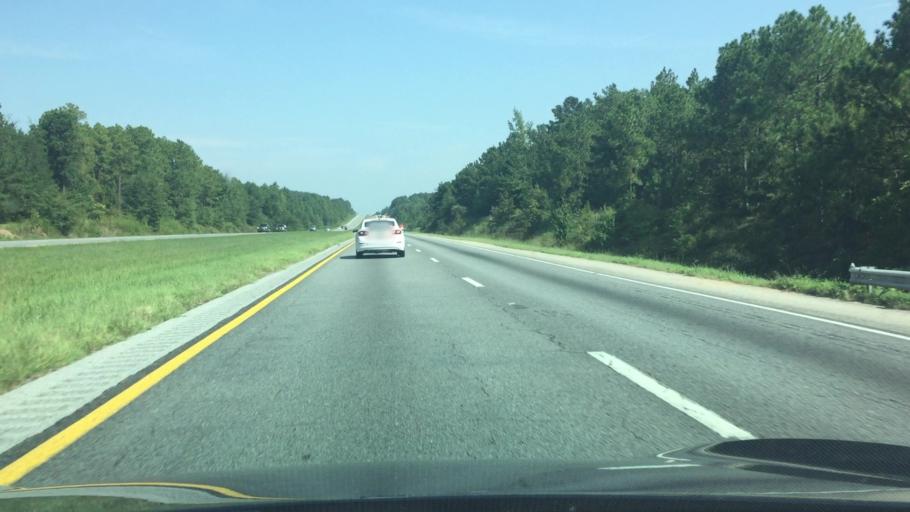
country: US
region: Alabama
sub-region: Autauga County
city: Marbury
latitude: 32.6889
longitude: -86.5156
